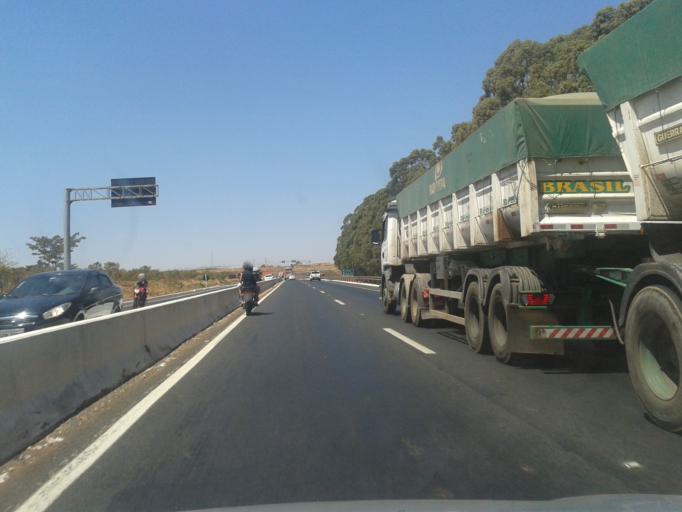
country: BR
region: Minas Gerais
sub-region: Uberlandia
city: Uberlandia
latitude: -18.9071
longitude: -48.2287
